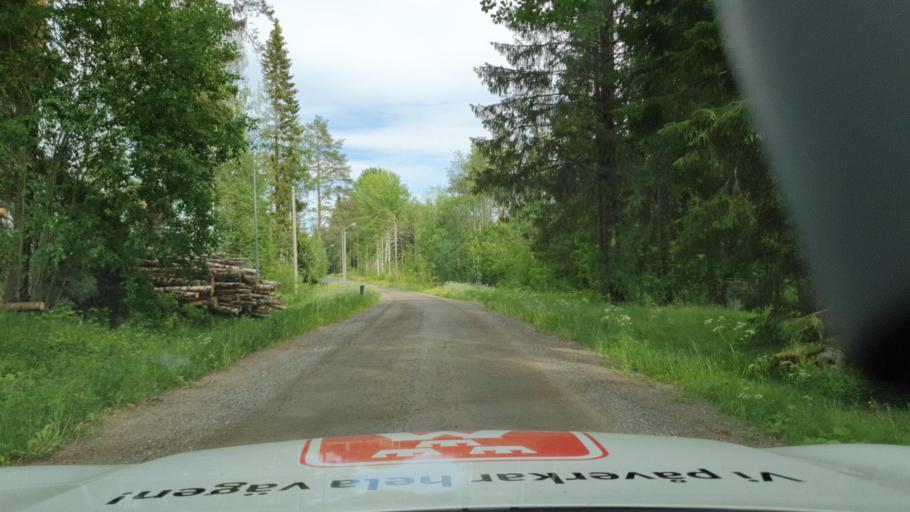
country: SE
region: Vaesterbotten
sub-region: Robertsfors Kommun
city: Robertsfors
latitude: 64.3730
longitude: 21.0509
